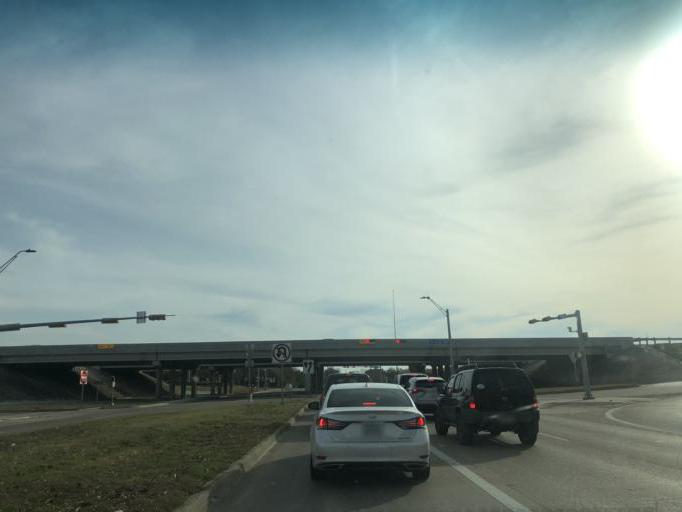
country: US
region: Texas
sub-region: Tarrant County
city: Dalworthington Gardens
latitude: 32.6755
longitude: -97.1497
